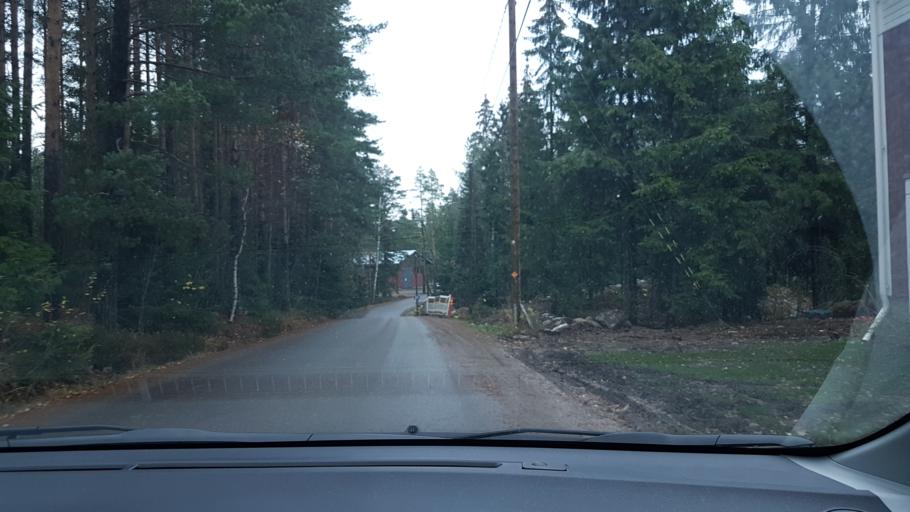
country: FI
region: Uusimaa
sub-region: Helsinki
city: Vantaa
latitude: 60.2825
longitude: 25.1579
